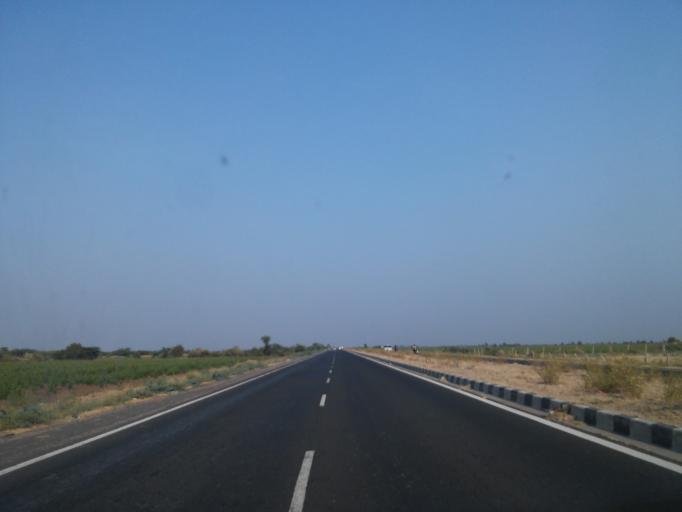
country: IN
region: Gujarat
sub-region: Surendranagar
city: Dhrangadhra
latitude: 23.0329
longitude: 71.6634
